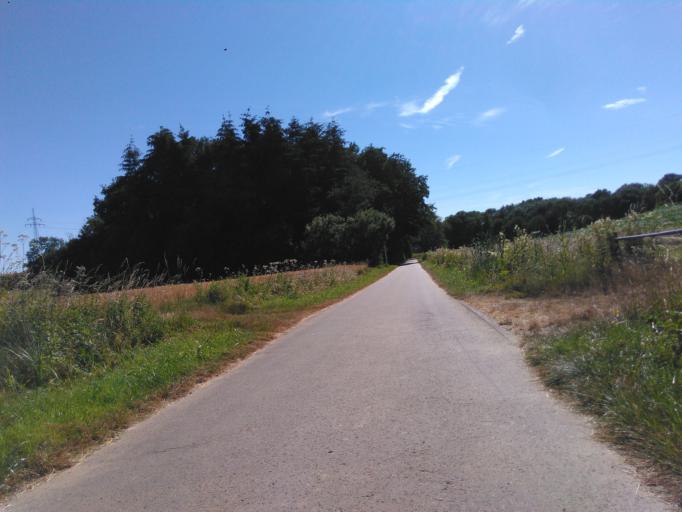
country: LU
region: Luxembourg
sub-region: Canton d'Esch-sur-Alzette
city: Sanem
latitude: 49.5517
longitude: 5.9424
